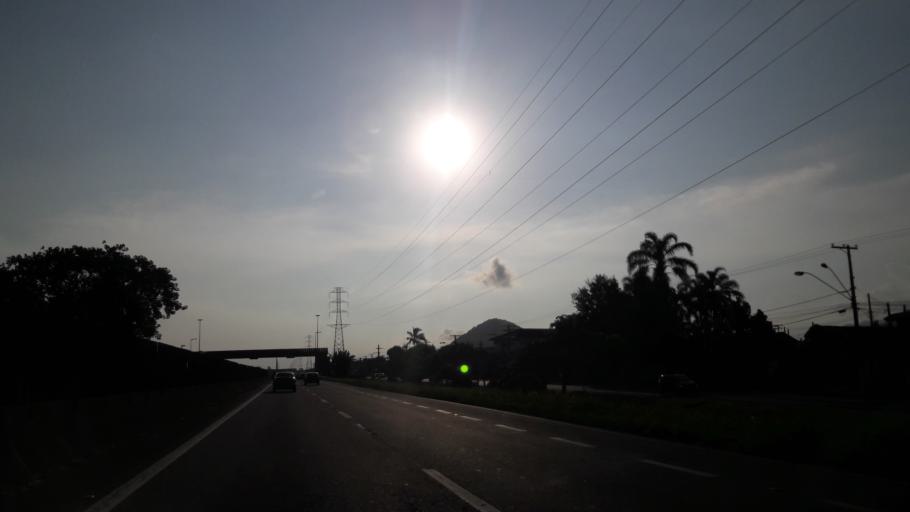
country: BR
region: Sao Paulo
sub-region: Mongagua
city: Mongagua
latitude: -24.1101
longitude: -46.6543
